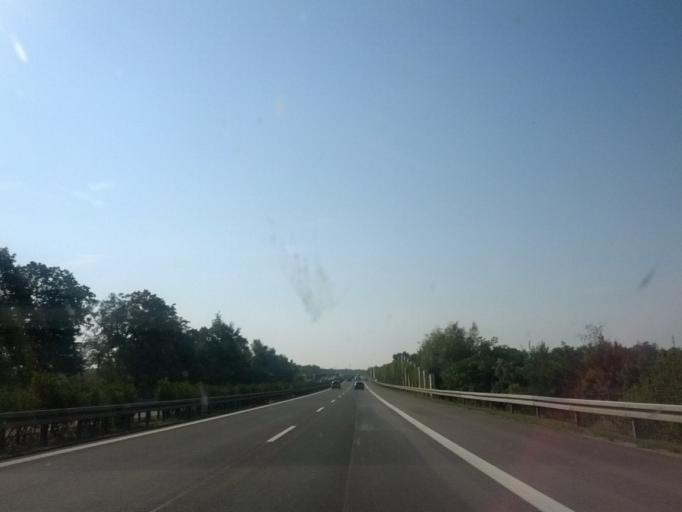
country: DE
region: Brandenburg
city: Bernau bei Berlin
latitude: 52.6763
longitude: 13.5651
